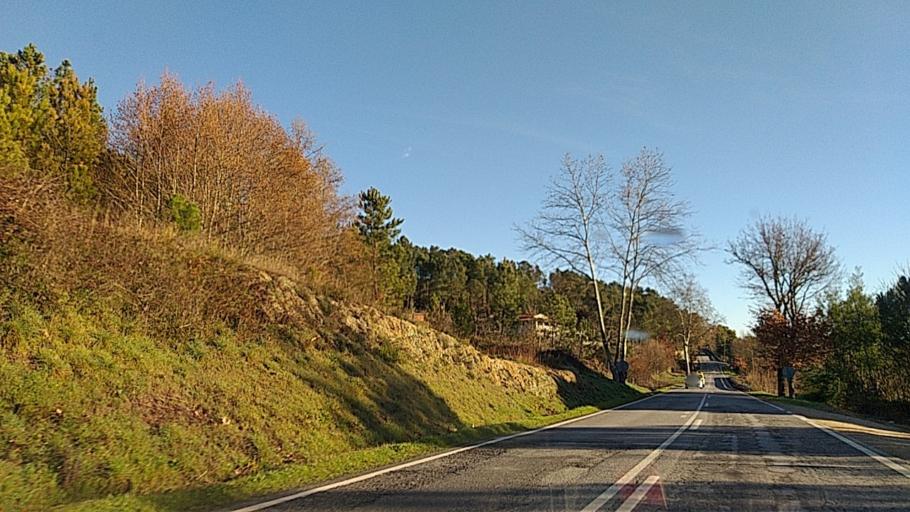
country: PT
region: Guarda
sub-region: Seia
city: Seia
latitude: 40.4344
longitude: -7.7138
